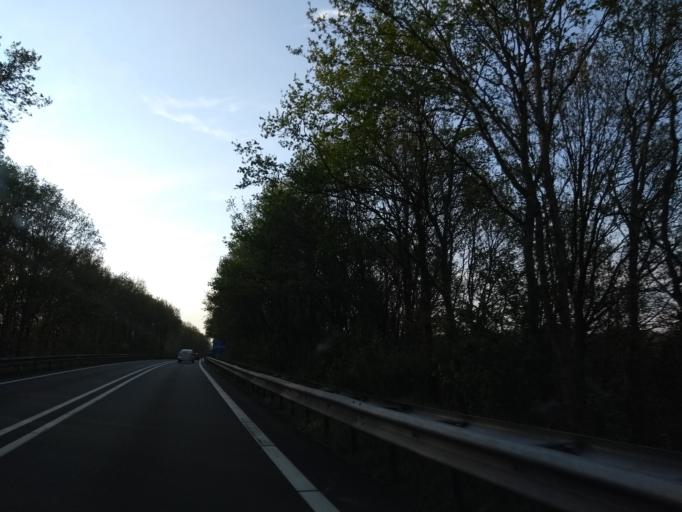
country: NL
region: Overijssel
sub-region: Gemeente Twenterand
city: Vroomshoop
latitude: 52.5051
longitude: 6.5686
